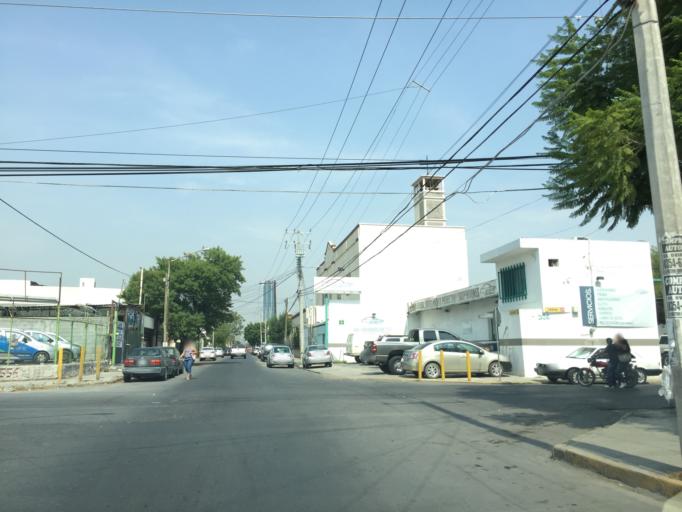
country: MX
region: Nuevo Leon
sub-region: Monterrey
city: Monterrey
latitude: 25.6614
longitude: -100.2998
